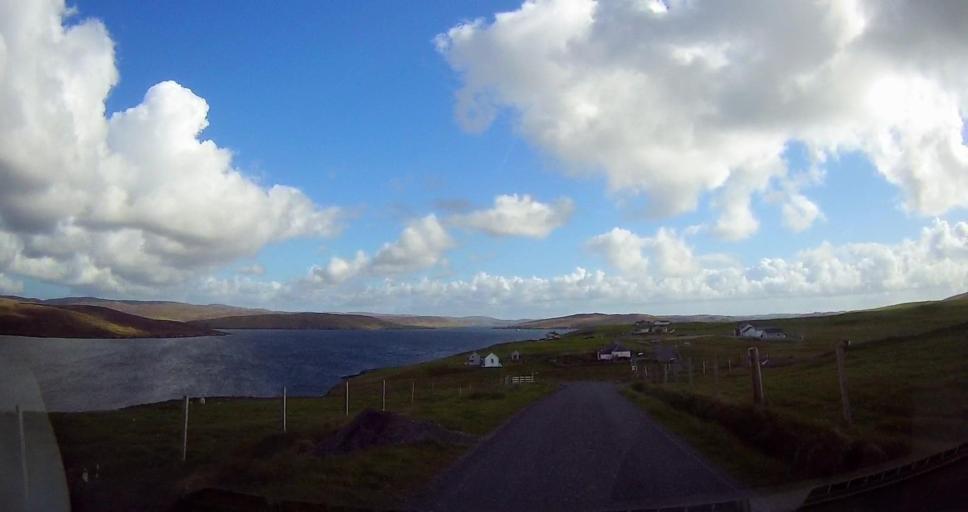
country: GB
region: Scotland
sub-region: Shetland Islands
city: Lerwick
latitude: 60.3673
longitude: -1.3817
